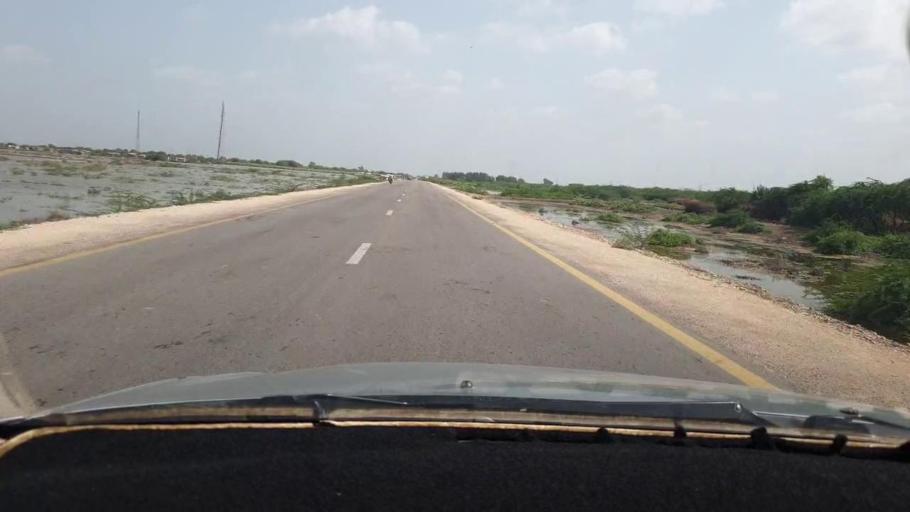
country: PK
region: Sindh
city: Digri
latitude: 25.1181
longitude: 69.1532
